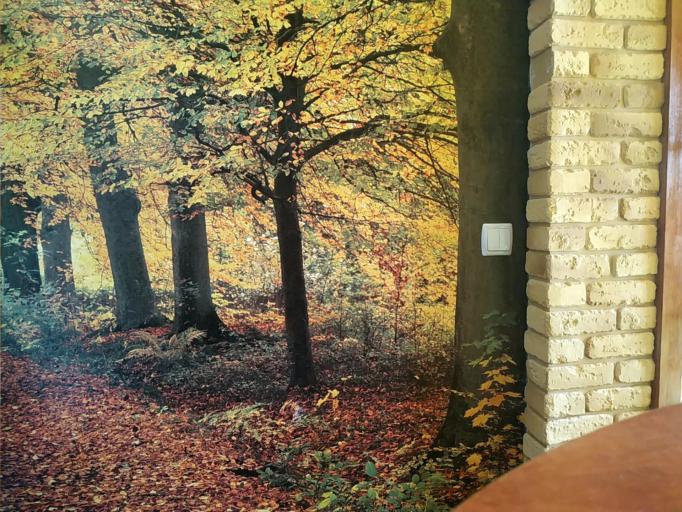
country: RU
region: Jaroslavl
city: Kukoboy
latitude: 58.9004
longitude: 39.6938
